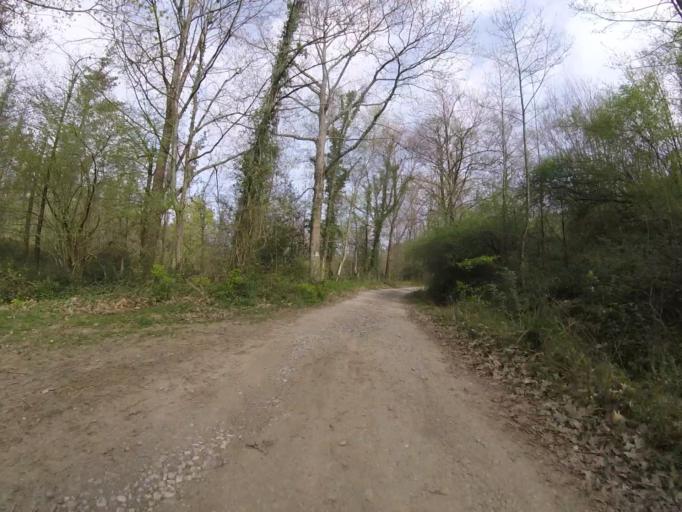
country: ES
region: Basque Country
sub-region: Provincia de Guipuzcoa
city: Usurbil
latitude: 43.2463
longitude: -2.0842
